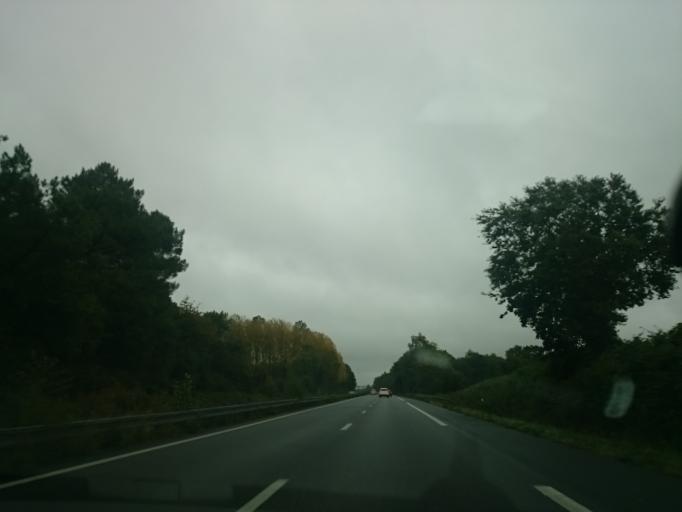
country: FR
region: Brittany
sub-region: Departement du Morbihan
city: Nostang
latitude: 47.7686
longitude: -3.1676
